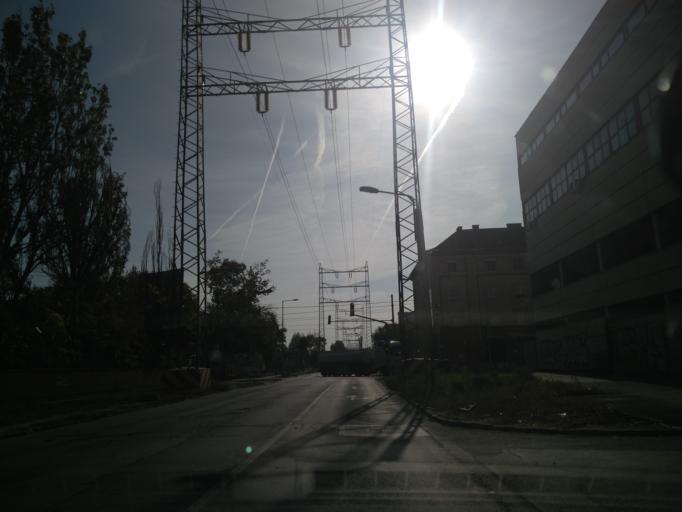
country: HU
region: Budapest
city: Budapest XIX. keruelet
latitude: 47.4763
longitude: 19.1185
